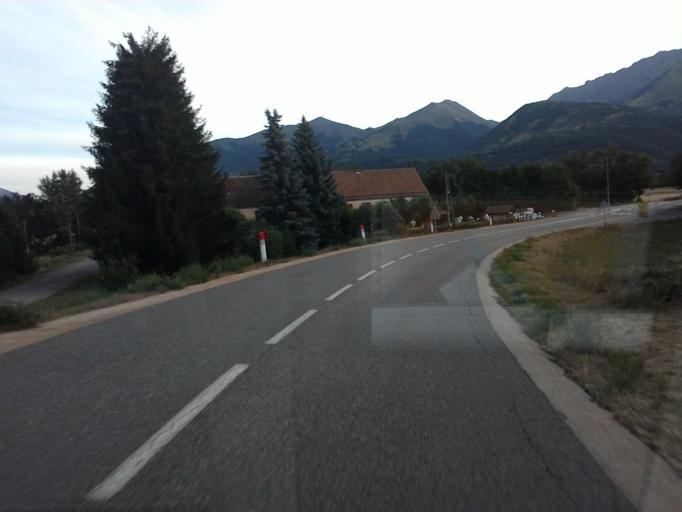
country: FR
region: Provence-Alpes-Cote d'Azur
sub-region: Departement des Hautes-Alpes
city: Saint-Bonnet-en-Champsaur
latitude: 44.7570
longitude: 6.0069
